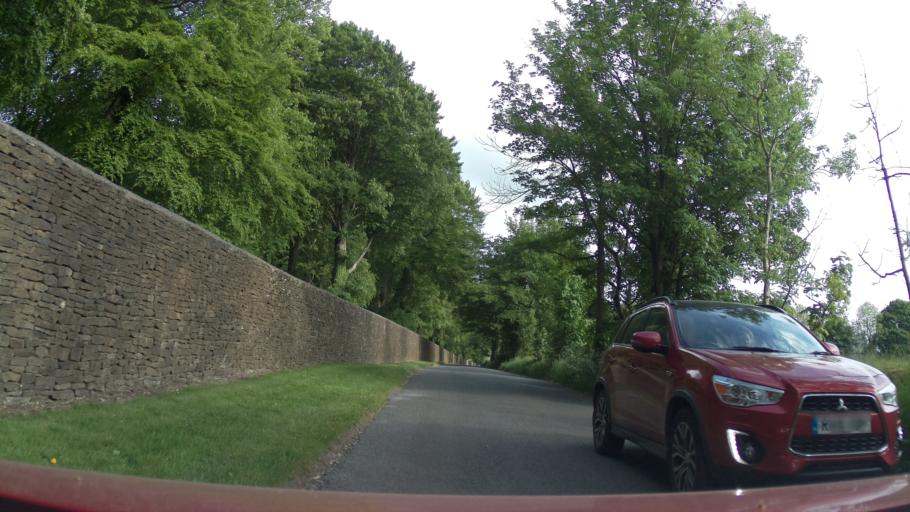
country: GB
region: England
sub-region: Gloucestershire
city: Westfield
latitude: 51.8763
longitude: -1.9034
